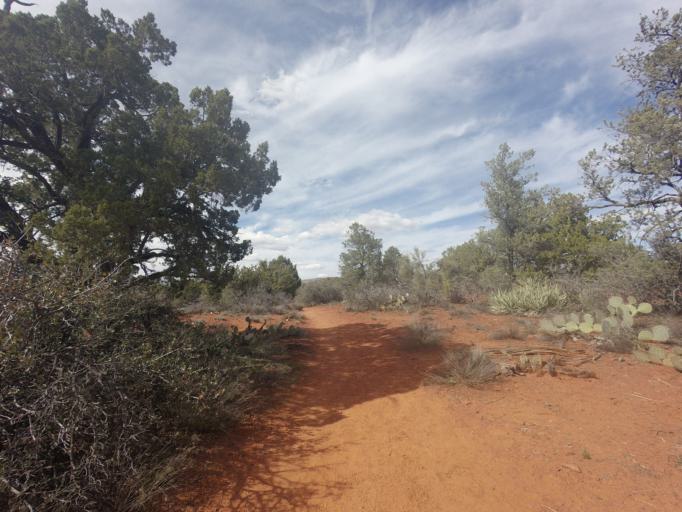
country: US
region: Arizona
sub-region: Yavapai County
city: West Sedona
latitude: 34.8070
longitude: -111.8323
